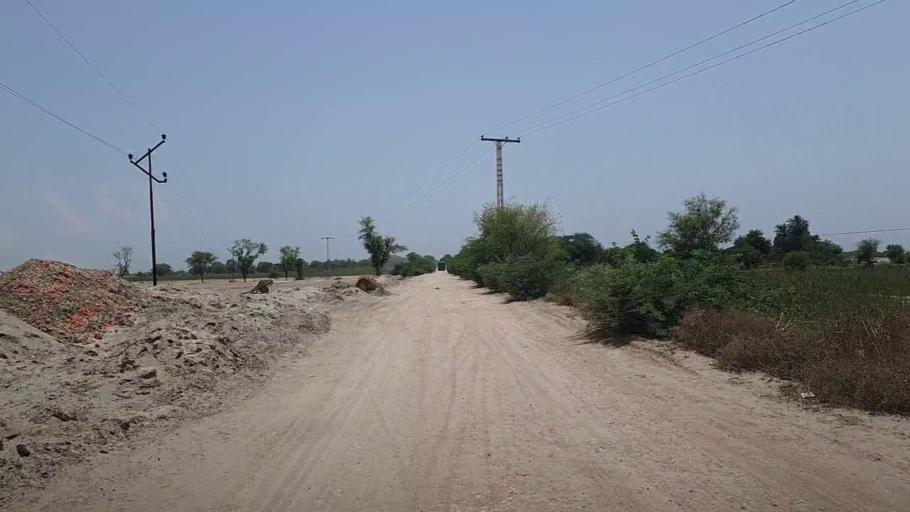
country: PK
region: Sindh
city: Pad Idan
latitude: 26.7631
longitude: 68.2936
